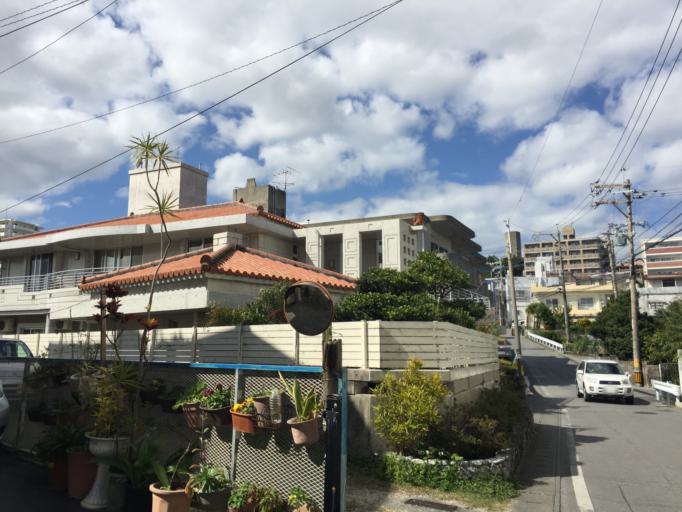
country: JP
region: Okinawa
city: Ginowan
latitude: 26.2354
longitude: 127.7333
